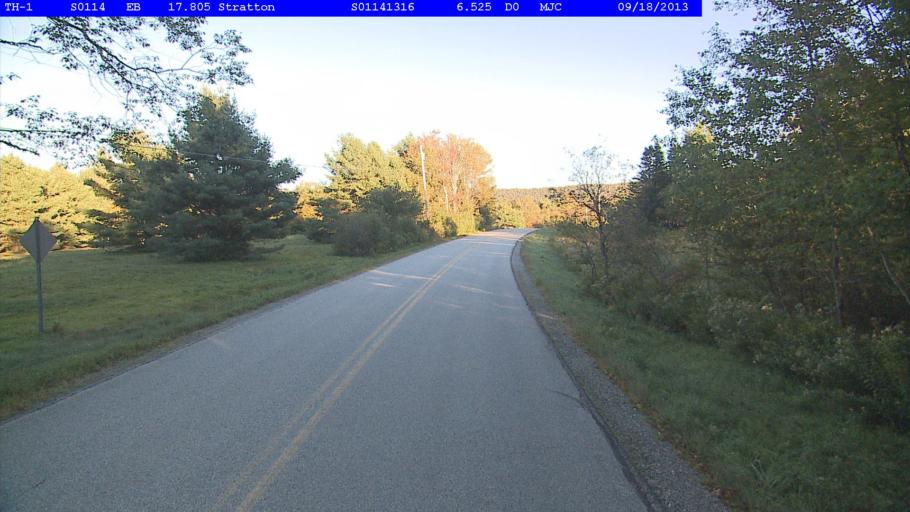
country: US
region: Vermont
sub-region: Windham County
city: Dover
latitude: 43.0316
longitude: -72.8901
